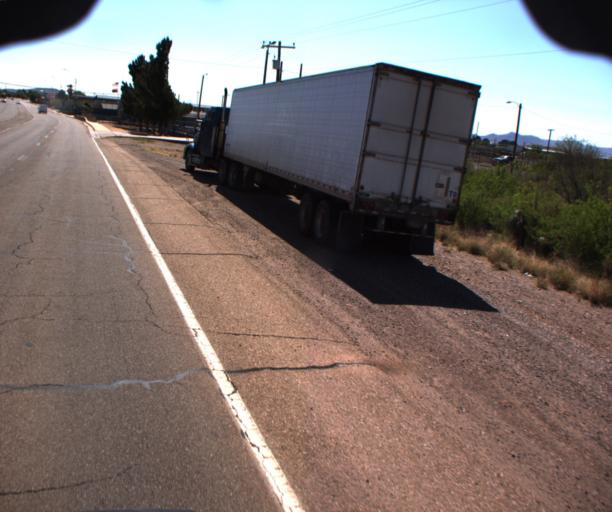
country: US
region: Arizona
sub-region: Cochise County
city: Pirtleville
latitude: 31.3507
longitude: -109.5638
